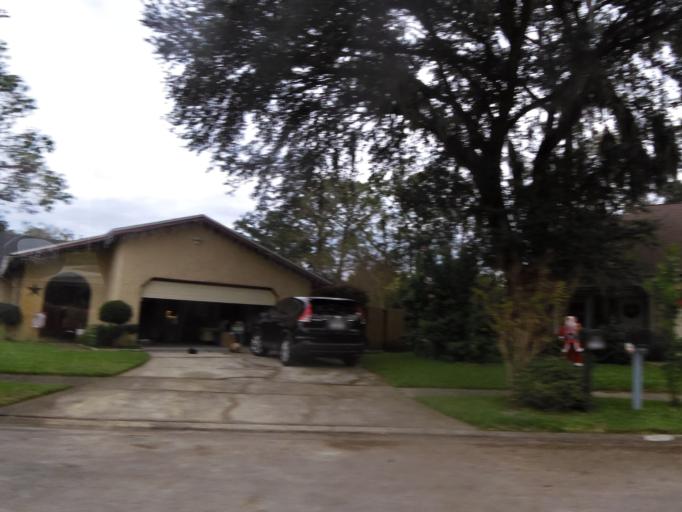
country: US
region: Florida
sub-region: Duval County
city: Jacksonville
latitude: 30.2682
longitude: -81.5996
